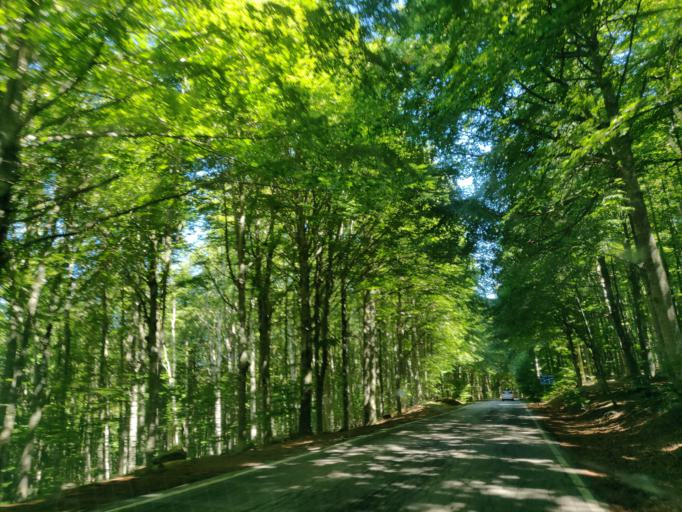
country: IT
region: Tuscany
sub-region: Provincia di Siena
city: Abbadia San Salvatore
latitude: 42.9023
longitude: 11.6167
